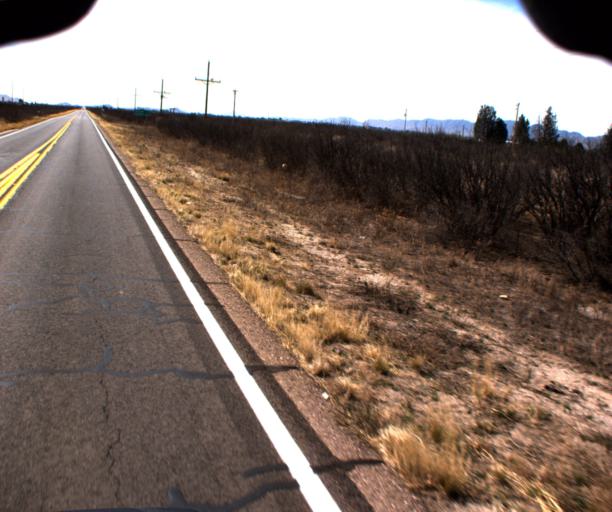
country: US
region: Arizona
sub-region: Cochise County
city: Willcox
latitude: 32.0328
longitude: -109.8774
